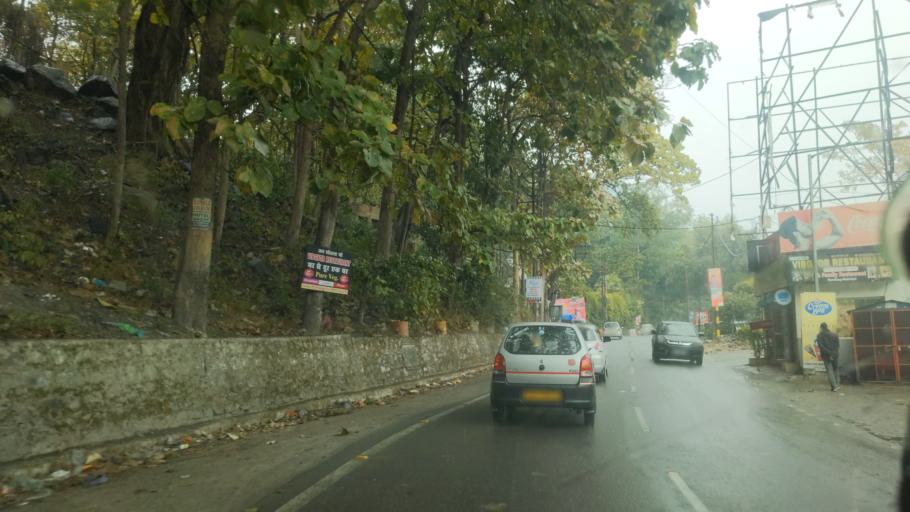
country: IN
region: Uttarakhand
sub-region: Naini Tal
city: Haldwani
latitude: 29.2818
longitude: 79.5448
